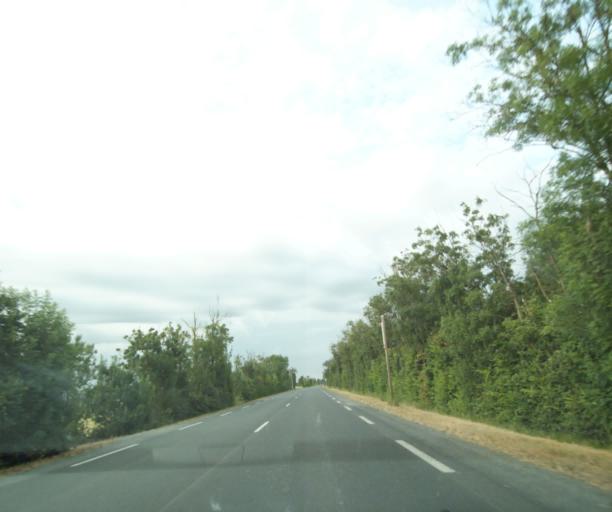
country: FR
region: Poitou-Charentes
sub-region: Departement de la Charente-Maritime
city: Marans
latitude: 46.3554
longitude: -0.9930
